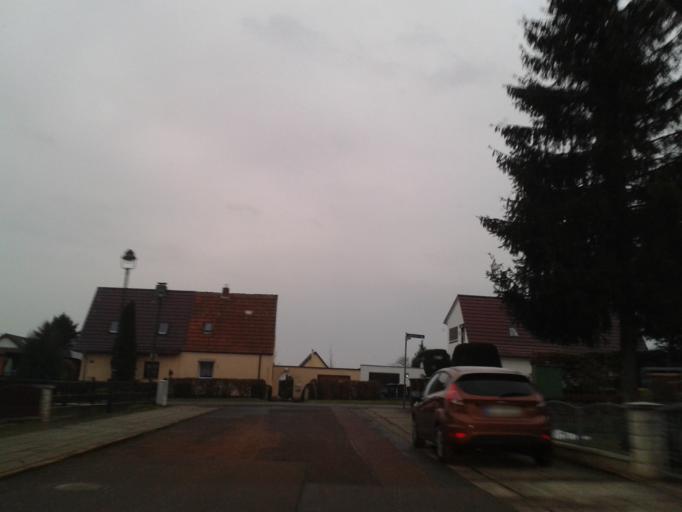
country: DE
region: Saxony-Anhalt
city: Halle (Saale)
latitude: 51.4945
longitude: 12.0260
